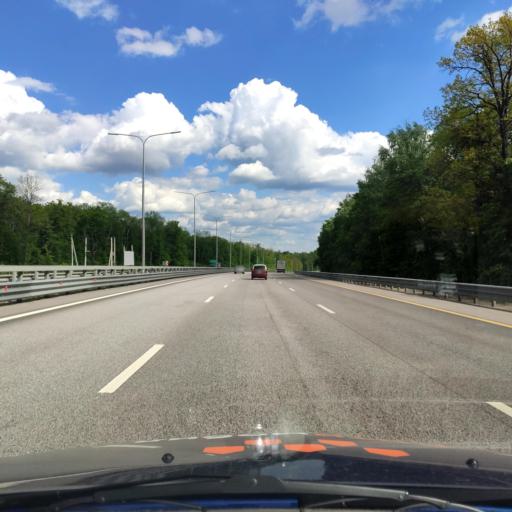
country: RU
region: Voronezj
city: Ramon'
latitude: 51.8318
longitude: 39.2383
